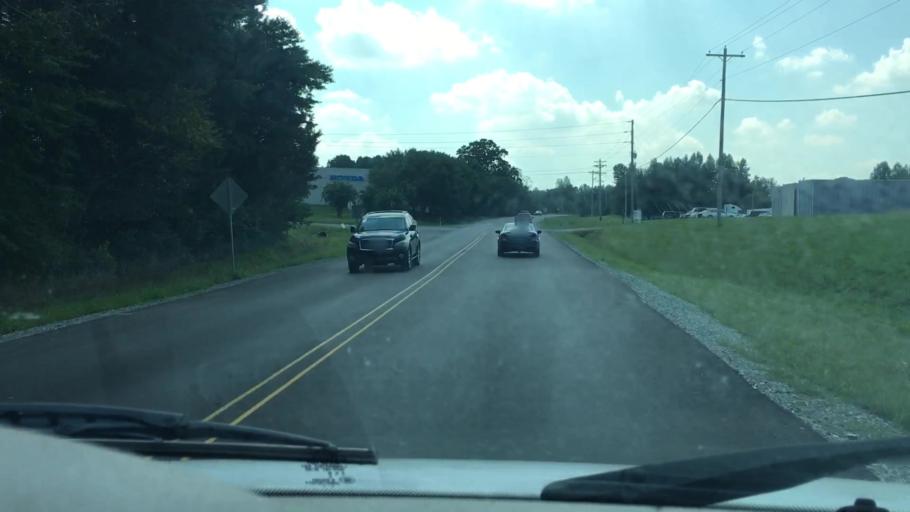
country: US
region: North Carolina
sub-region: Mecklenburg County
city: Huntersville
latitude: 35.3974
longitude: -80.8516
